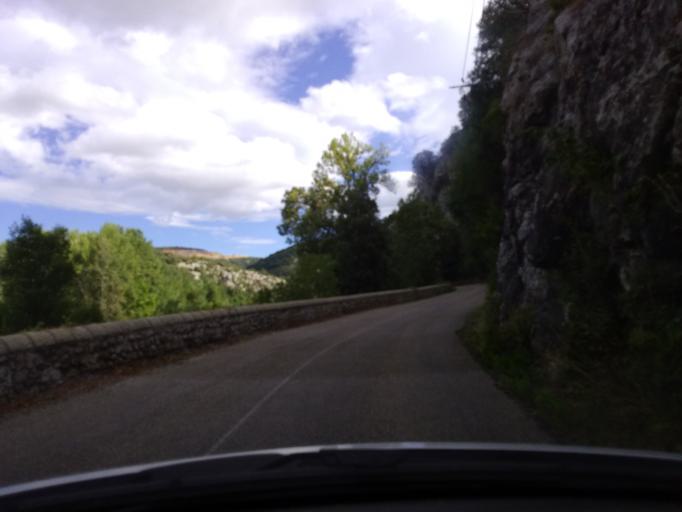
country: FR
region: Languedoc-Roussillon
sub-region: Departement de l'Herault
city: Saint-Bauzille-de-Putois
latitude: 43.8611
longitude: 3.7063
